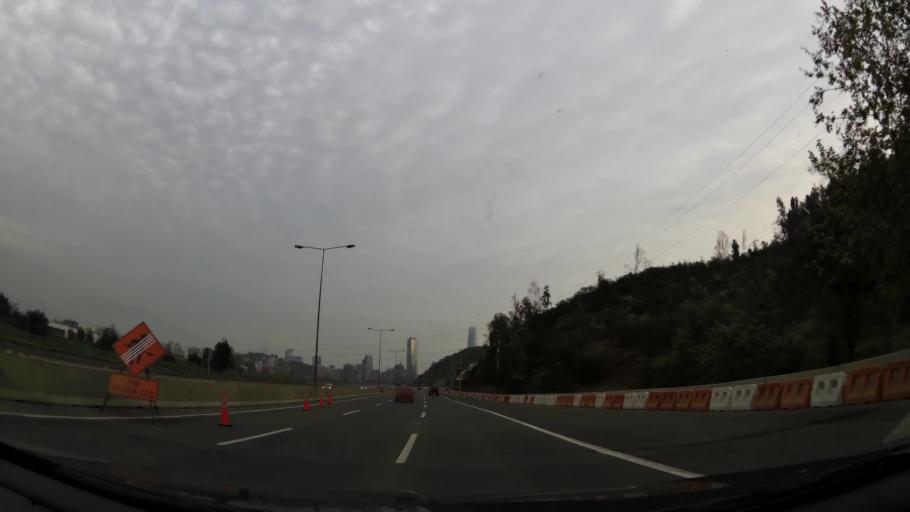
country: CL
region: Santiago Metropolitan
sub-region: Provincia de Santiago
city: Villa Presidente Frei, Nunoa, Santiago, Chile
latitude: -33.3972
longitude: -70.6046
